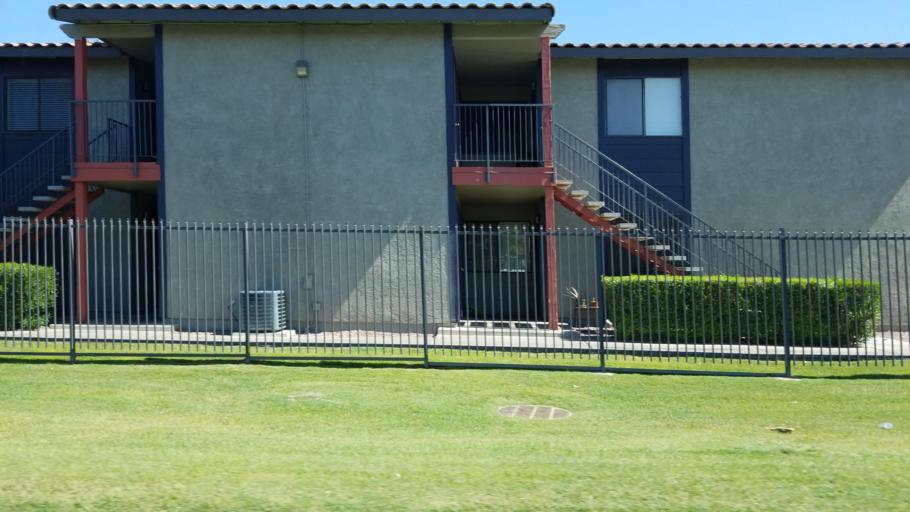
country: US
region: Arizona
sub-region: Maricopa County
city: Tolleson
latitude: 33.4945
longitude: -112.2341
